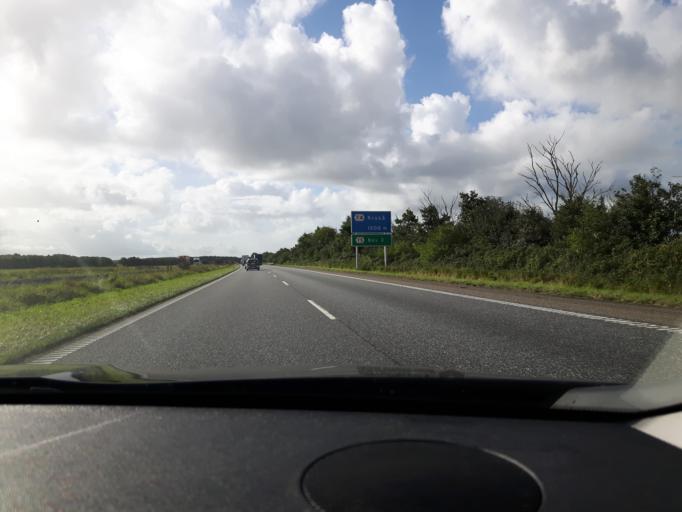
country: DK
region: South Denmark
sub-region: Aabenraa Kommune
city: Krusa
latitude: 54.8958
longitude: 9.3770
